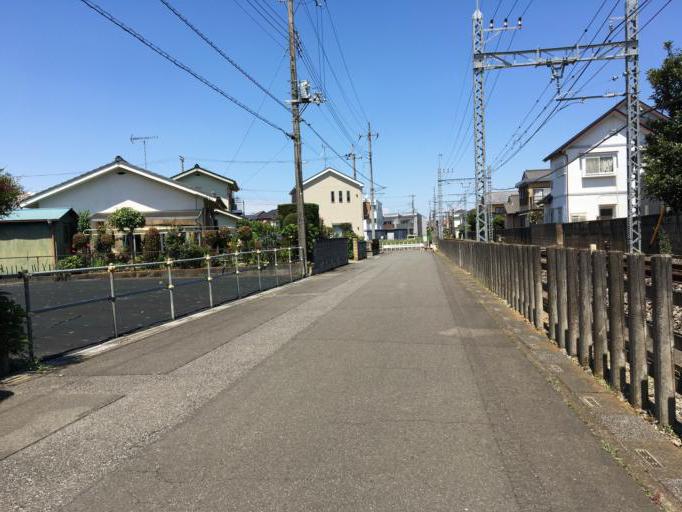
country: JP
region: Saitama
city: Sakado
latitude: 35.9504
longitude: 139.3838
